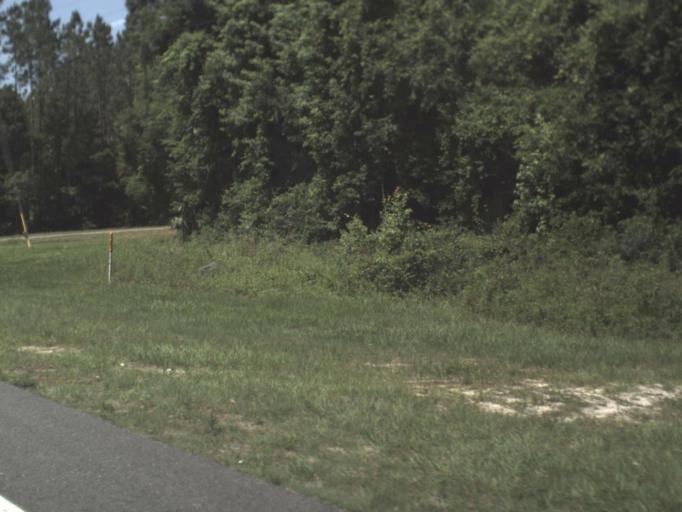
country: US
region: Florida
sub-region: Levy County
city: Williston
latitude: 29.4418
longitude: -82.4110
